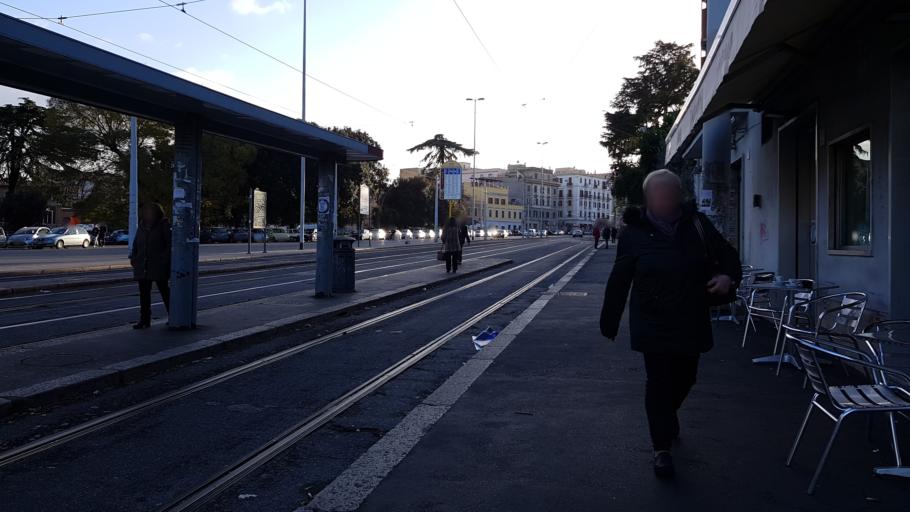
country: IT
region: Latium
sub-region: Citta metropolitana di Roma Capitale
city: Rome
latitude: 41.9017
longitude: 12.5186
